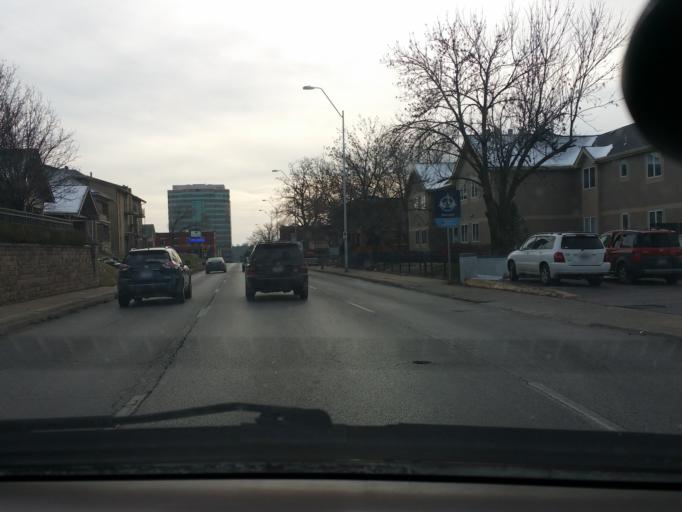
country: US
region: Kansas
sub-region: Johnson County
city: Westwood
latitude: 39.0498
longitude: -94.5981
